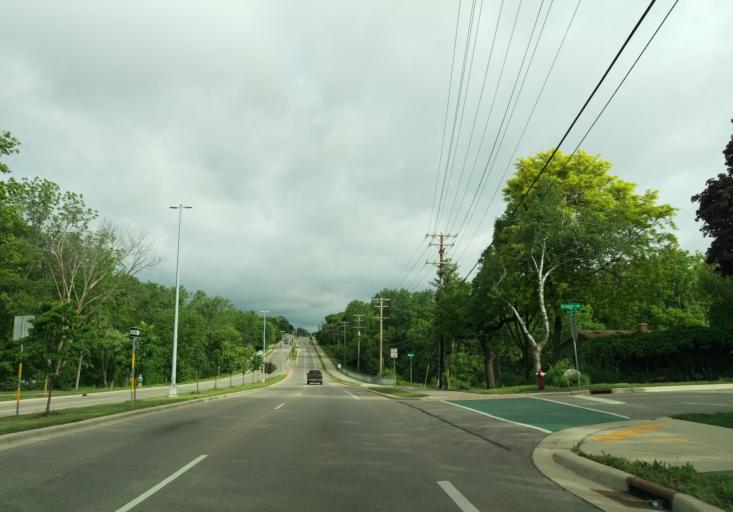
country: US
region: Wisconsin
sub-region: Dane County
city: Middleton
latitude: 43.0857
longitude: -89.4792
